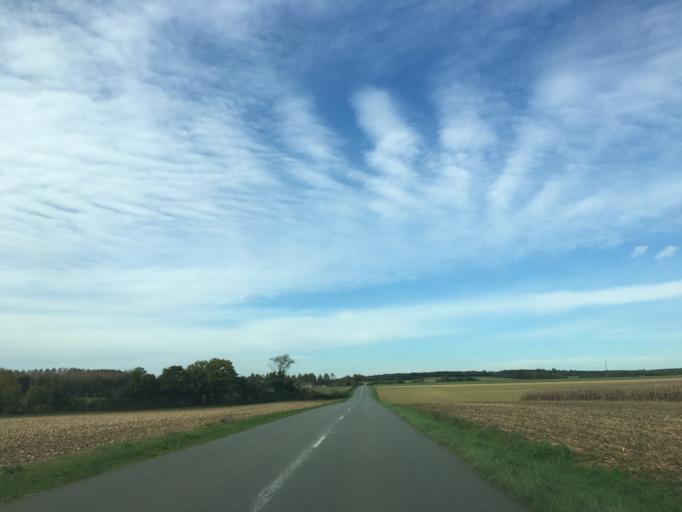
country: FR
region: Poitou-Charentes
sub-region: Departement de la Charente-Maritime
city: Aulnay
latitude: 46.0688
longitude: -0.4240
